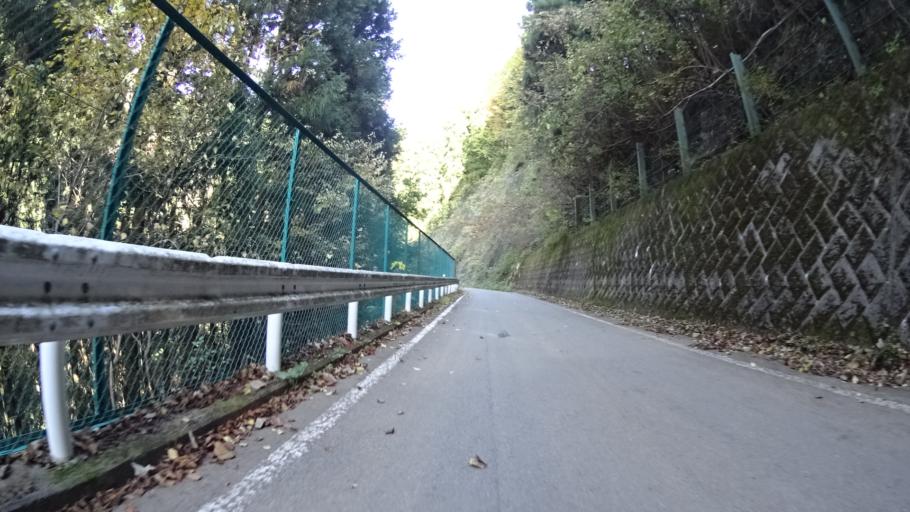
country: JP
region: Yamanashi
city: Uenohara
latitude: 35.6572
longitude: 139.1609
